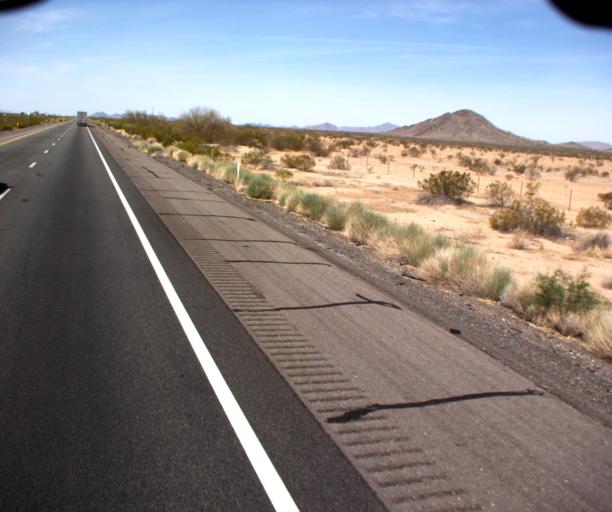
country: US
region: Arizona
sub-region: La Paz County
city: Salome
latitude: 33.5819
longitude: -113.4365
